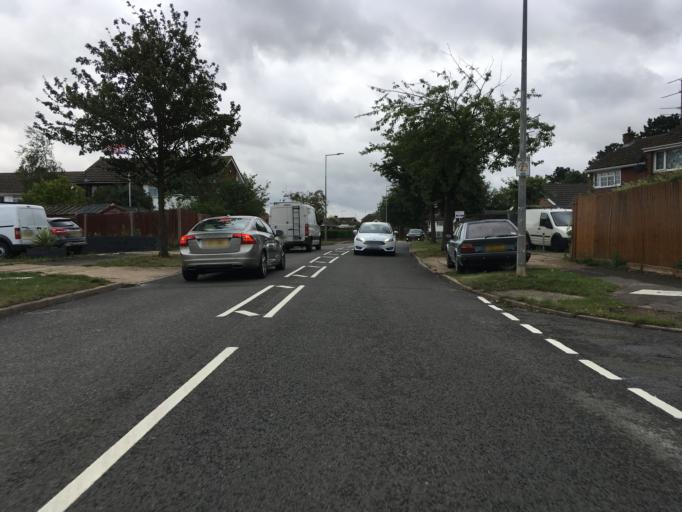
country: GB
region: England
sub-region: Buckinghamshire
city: Bletchley
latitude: 52.0053
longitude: -0.7420
